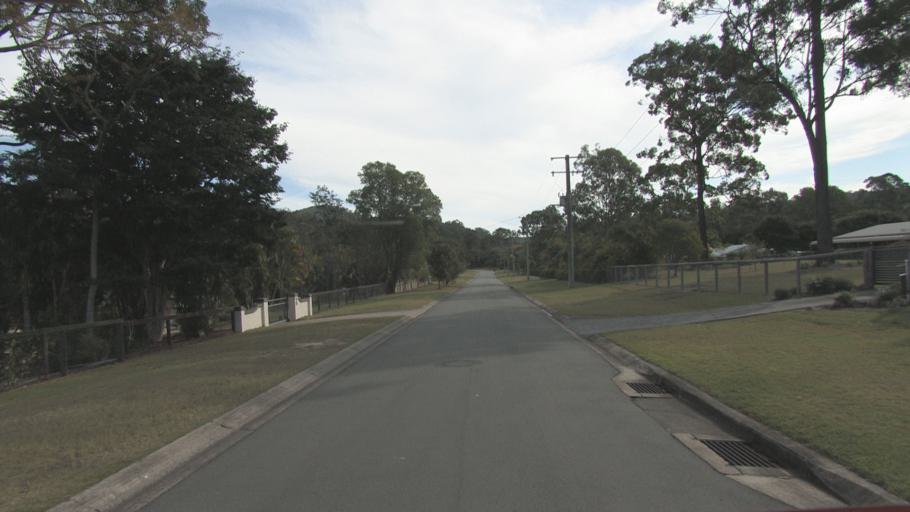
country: AU
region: Queensland
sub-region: Logan
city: Windaroo
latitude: -27.7603
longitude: 153.1904
